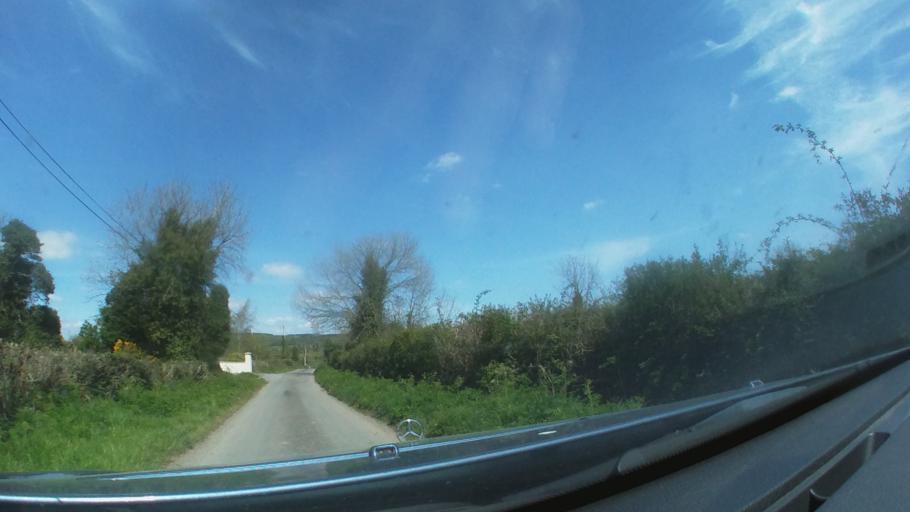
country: IE
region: Leinster
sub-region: Kilkenny
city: Callan
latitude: 52.6200
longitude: -7.4883
